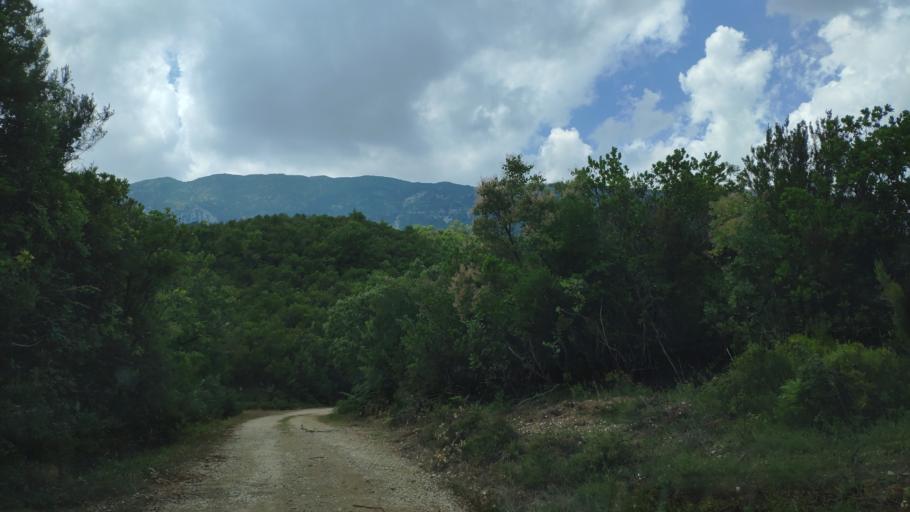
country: GR
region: Epirus
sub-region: Nomos Artas
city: Agios Dimitrios
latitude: 39.3189
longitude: 21.0102
